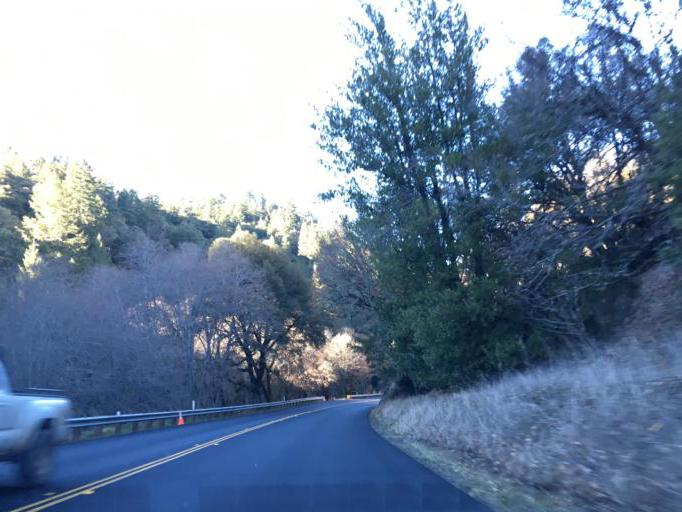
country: US
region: California
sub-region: Mendocino County
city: Laytonville
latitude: 39.8170
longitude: -123.5632
